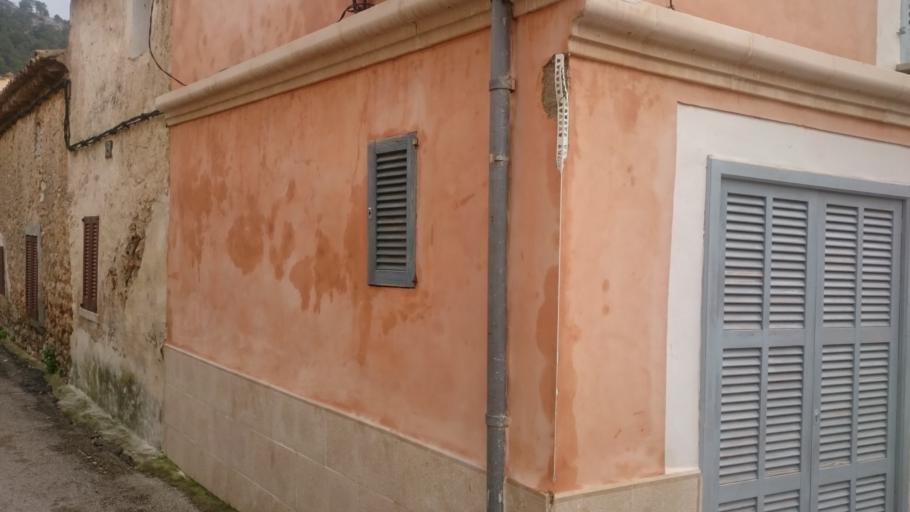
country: ES
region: Balearic Islands
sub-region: Illes Balears
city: Alaro
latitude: 39.7069
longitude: 2.7824
